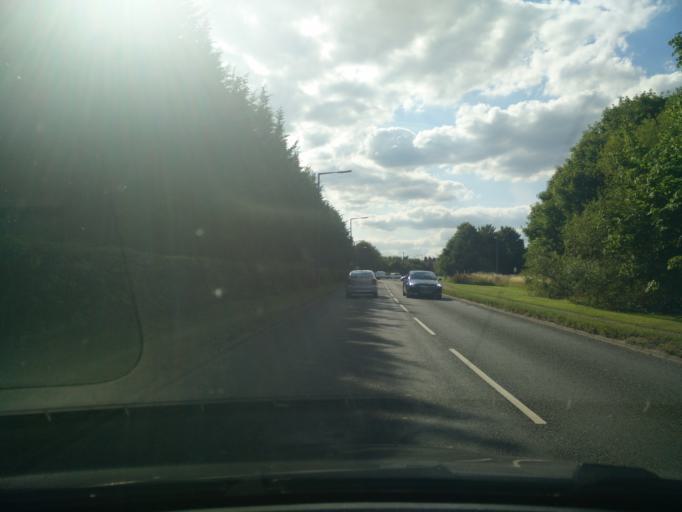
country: GB
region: England
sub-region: Derbyshire
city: Ilkeston
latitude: 52.9464
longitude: -1.3055
